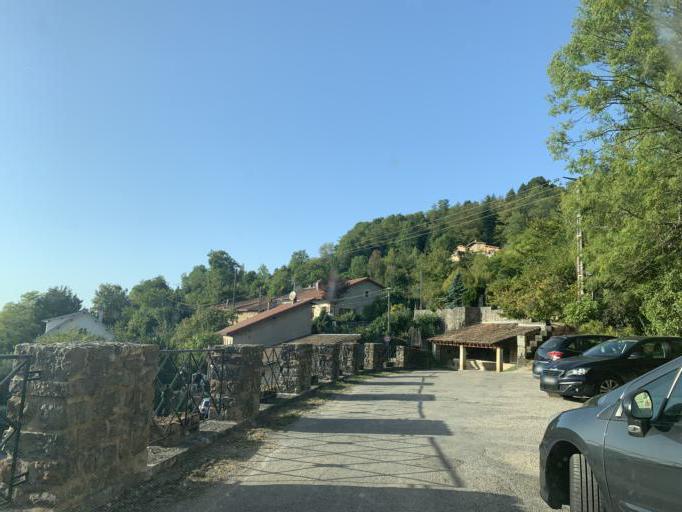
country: FR
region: Rhone-Alpes
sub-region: Departement de l'Ain
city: Vaux-en-Bugey
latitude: 45.9483
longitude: 5.3711
